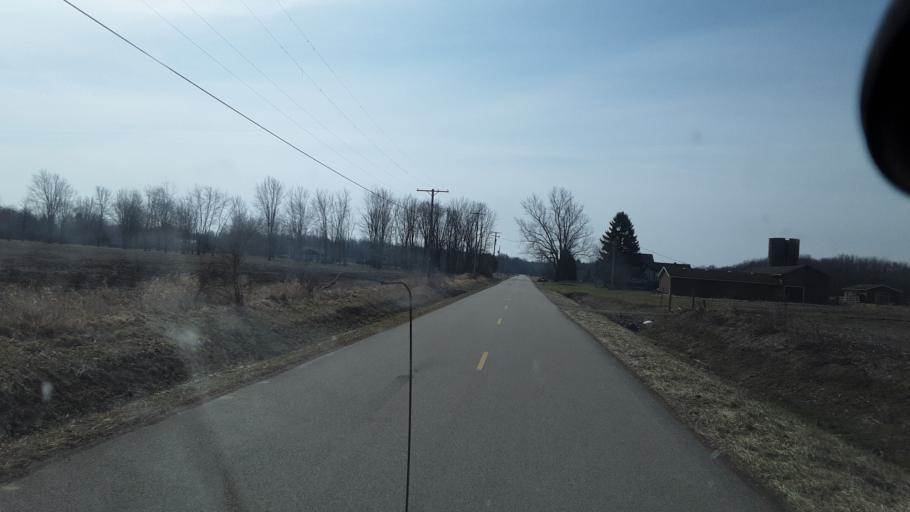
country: US
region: Ohio
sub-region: Ashtabula County
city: Jefferson
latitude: 41.7545
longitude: -80.7415
